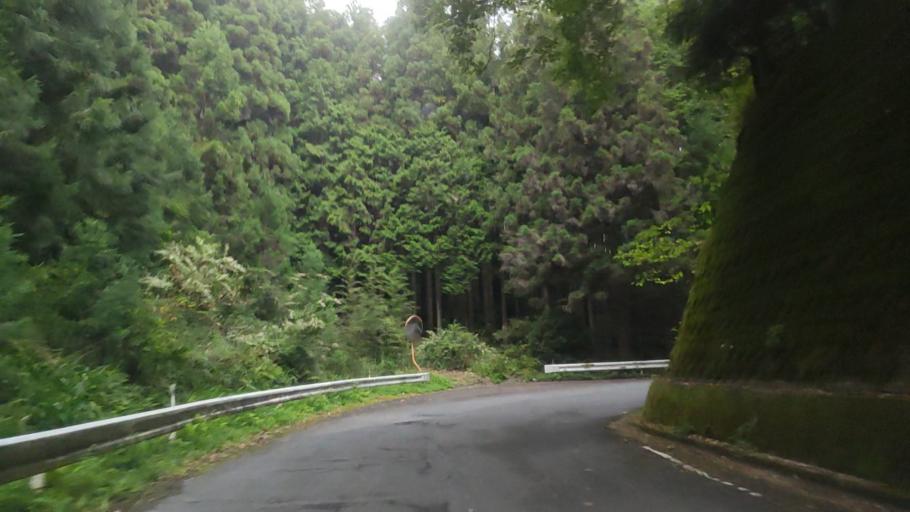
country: JP
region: Wakayama
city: Hashimoto
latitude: 34.2803
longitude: 135.6282
